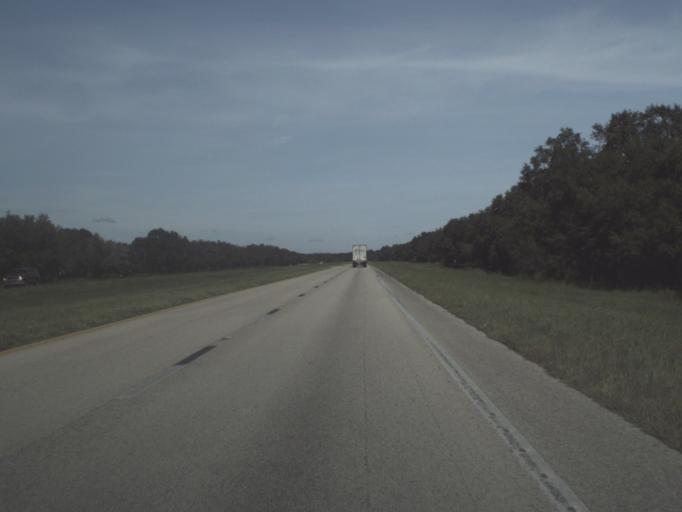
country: US
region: Florida
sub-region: Hendry County
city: Port LaBelle
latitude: 26.9614
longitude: -81.3164
